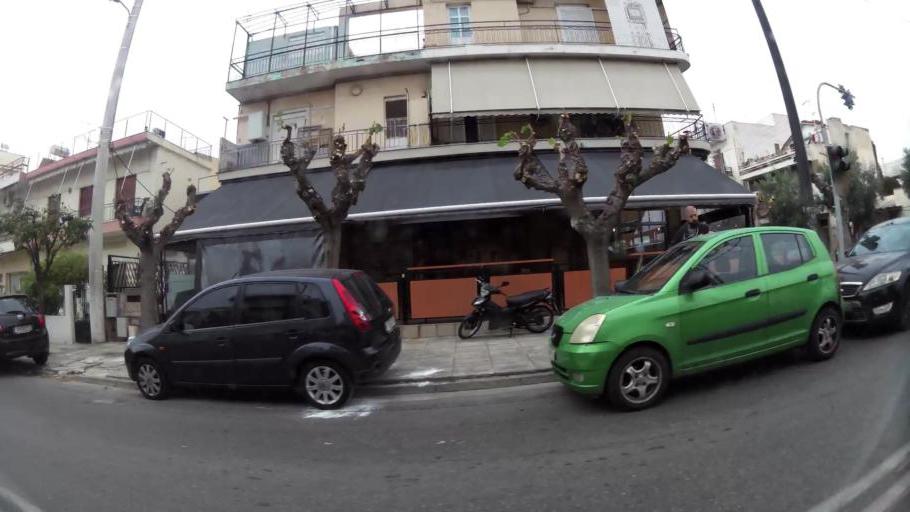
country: GR
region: Attica
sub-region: Nomarchia Athinas
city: Peristeri
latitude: 38.0112
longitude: 23.7029
